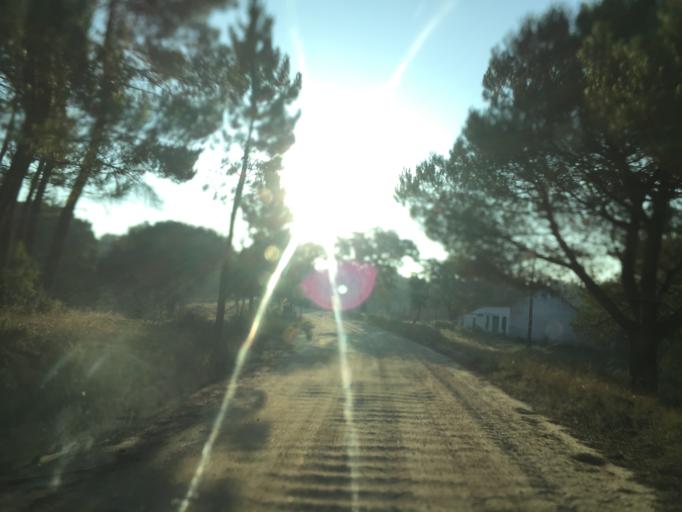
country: PT
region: Portalegre
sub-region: Ponte de Sor
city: Santo Andre
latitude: 39.0940
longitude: -8.3561
